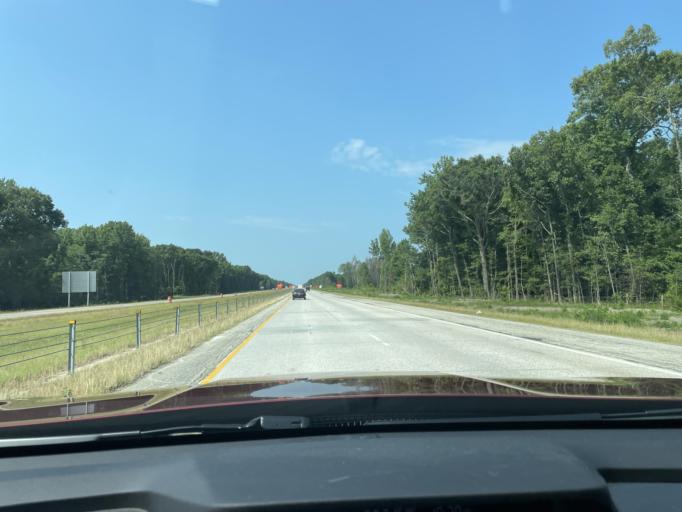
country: US
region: Arkansas
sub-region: White County
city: Searcy
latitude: 35.1892
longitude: -91.7492
